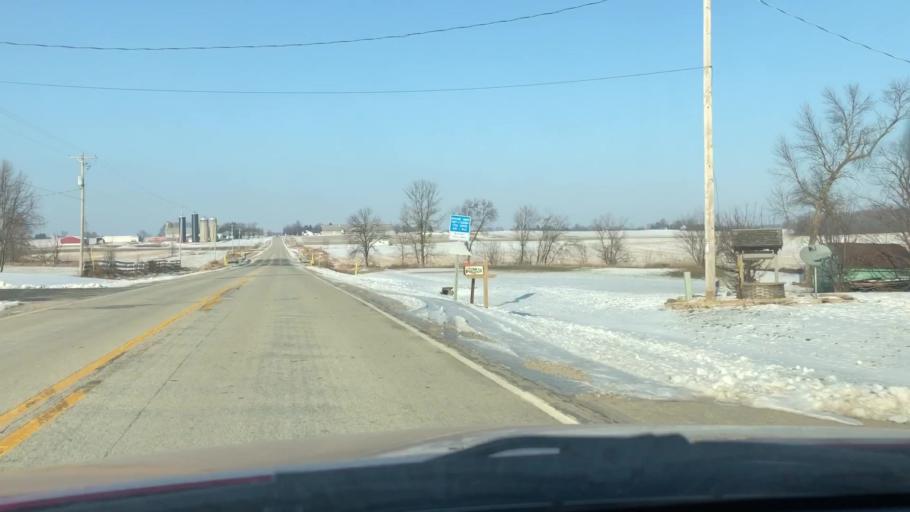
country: US
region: Wisconsin
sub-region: Outagamie County
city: Black Creek
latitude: 44.4022
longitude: -88.3744
